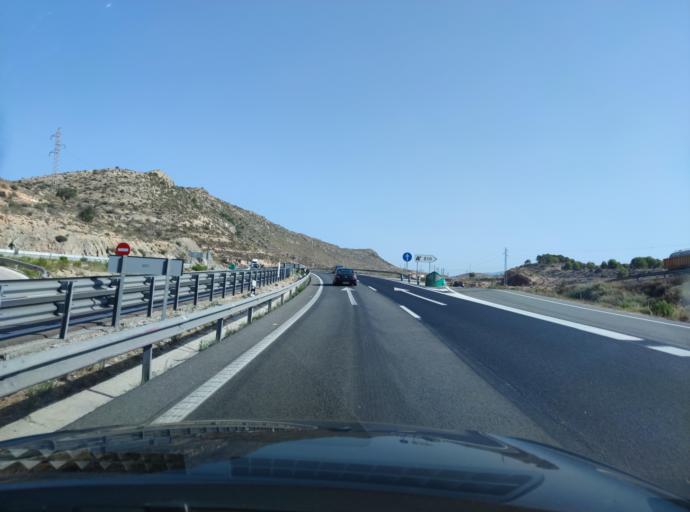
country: ES
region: Valencia
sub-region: Provincia de Alicante
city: Elda
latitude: 38.4318
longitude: -0.7823
